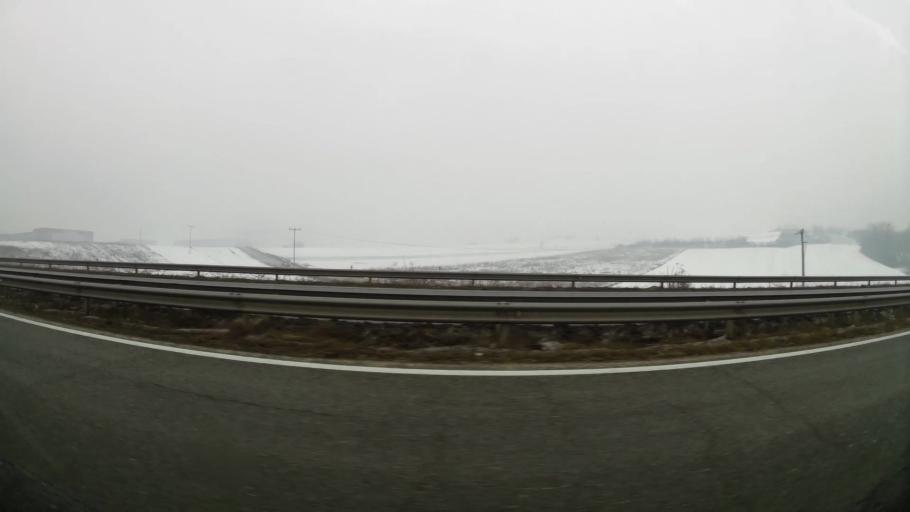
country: MK
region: Petrovec
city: Petrovec
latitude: 41.9437
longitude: 21.6296
